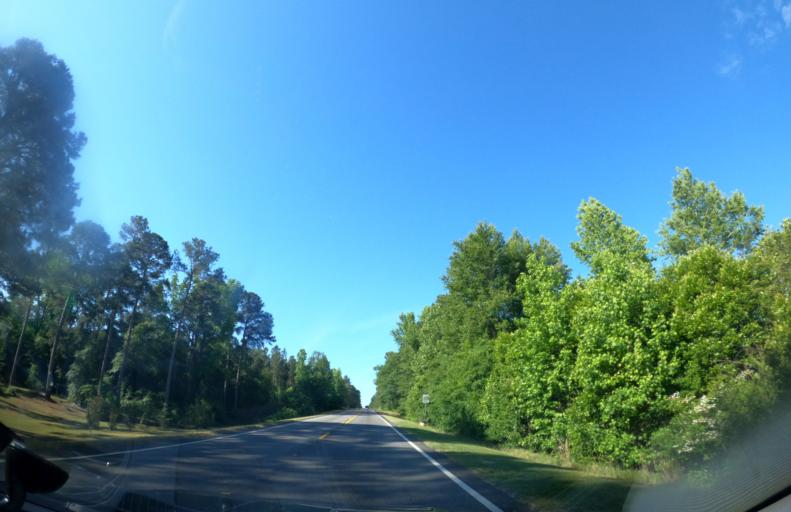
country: US
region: Georgia
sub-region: Columbia County
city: Harlem
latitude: 33.3755
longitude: -82.3213
